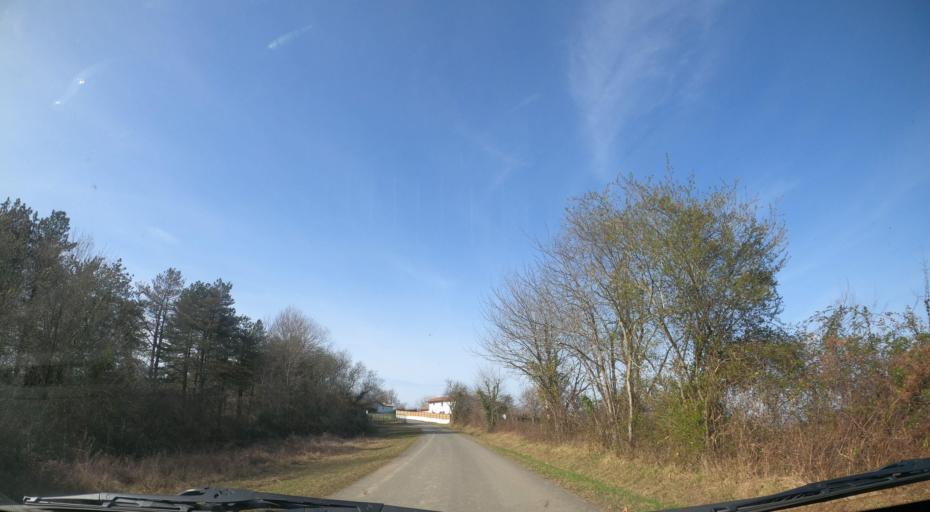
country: FR
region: Aquitaine
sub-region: Departement des Pyrenees-Atlantiques
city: Briscous
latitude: 43.4268
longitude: -1.3720
